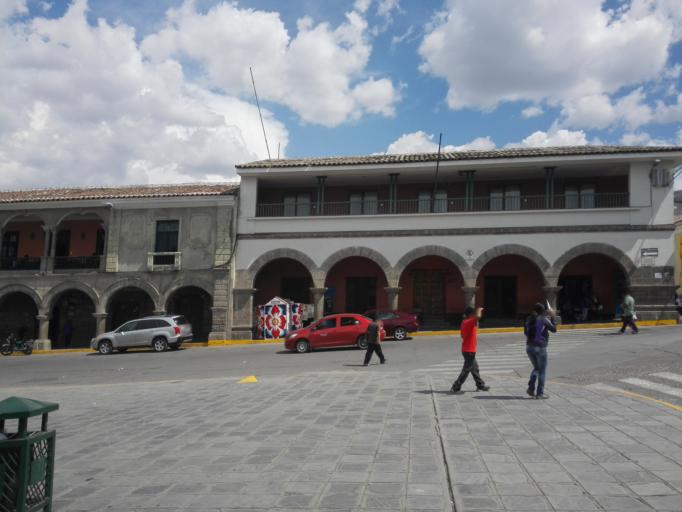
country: PE
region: Ayacucho
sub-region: Provincia de Huamanga
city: Ayacucho
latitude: -13.1606
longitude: -74.2263
